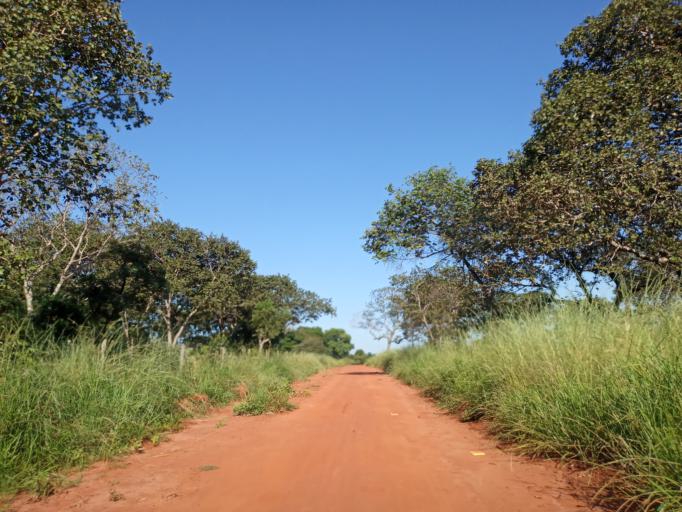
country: BR
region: Minas Gerais
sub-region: Ituiutaba
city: Ituiutaba
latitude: -18.9702
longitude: -49.4997
